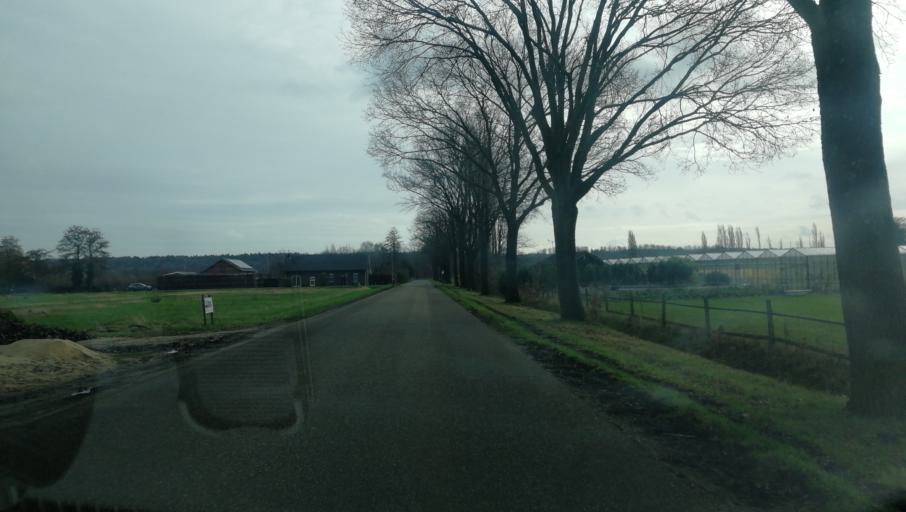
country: NL
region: Limburg
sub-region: Gemeente Beesel
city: Offenbeek
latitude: 51.3015
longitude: 6.1274
